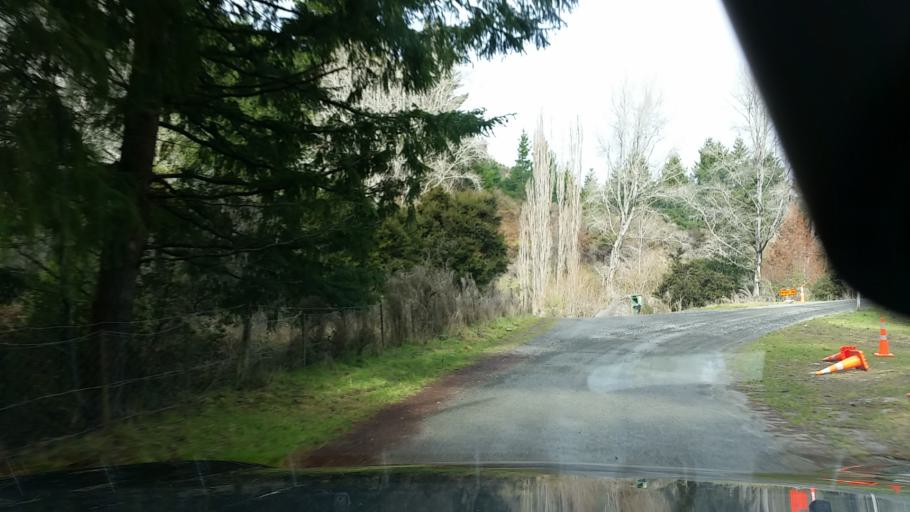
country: NZ
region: Tasman
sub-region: Tasman District
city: Richmond
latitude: -41.7291
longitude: 173.4696
